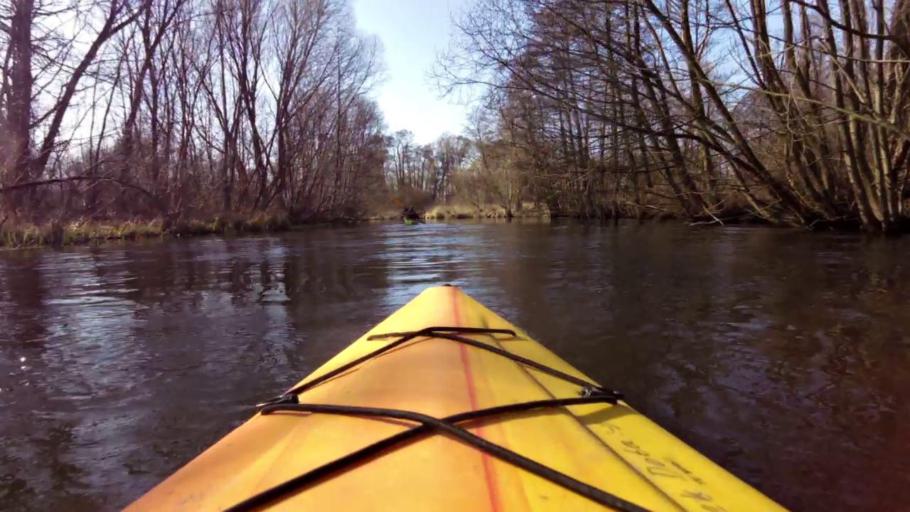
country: PL
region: West Pomeranian Voivodeship
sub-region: Powiat lobeski
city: Resko
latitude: 53.7687
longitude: 15.4070
